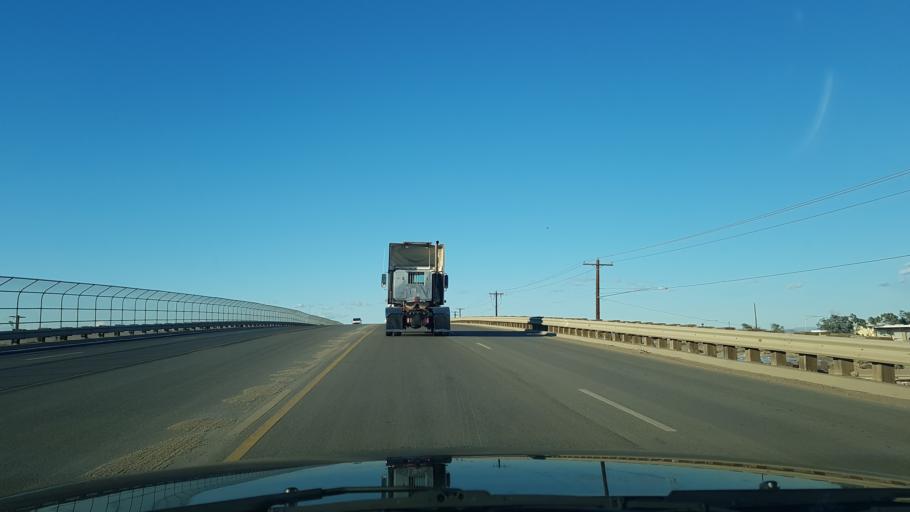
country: US
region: Arizona
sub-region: Yuma County
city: Yuma
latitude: 32.6869
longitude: -114.5988
